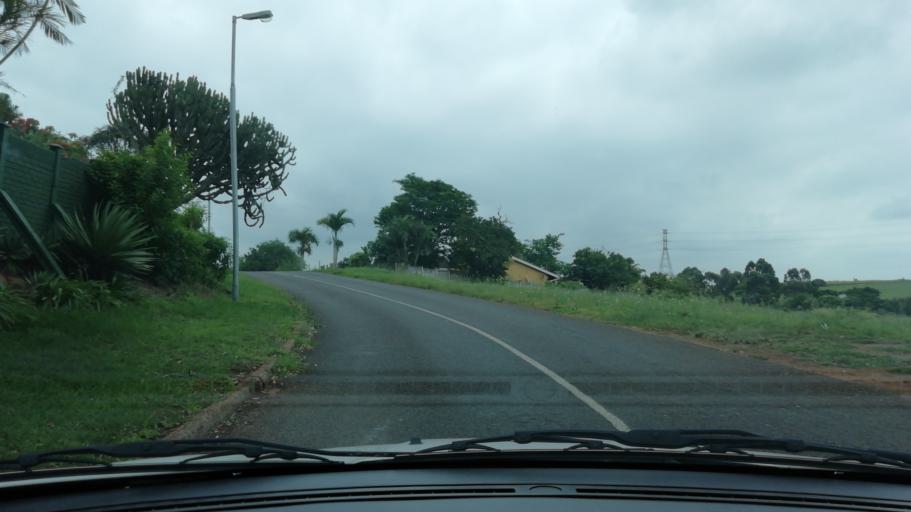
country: ZA
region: KwaZulu-Natal
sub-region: uThungulu District Municipality
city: Empangeni
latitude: -28.7353
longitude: 31.9022
